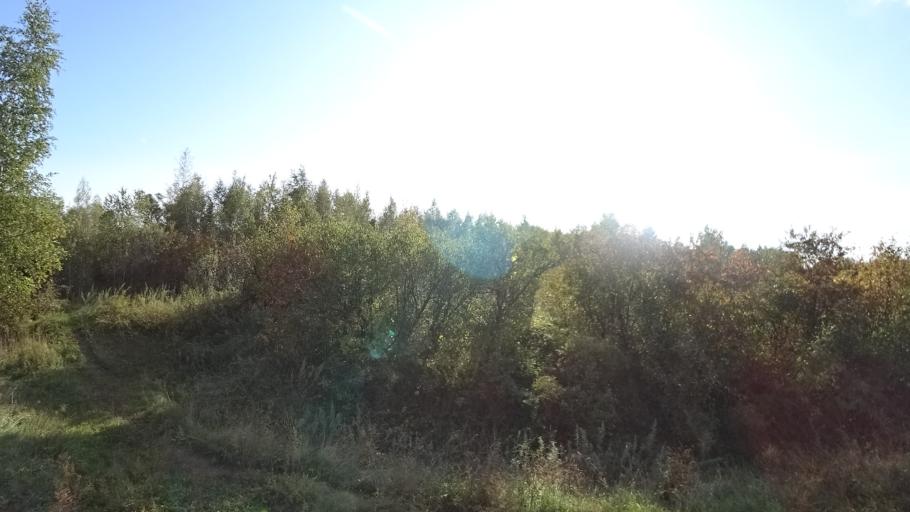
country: RU
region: Amur
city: Arkhara
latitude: 49.3486
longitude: 130.1162
